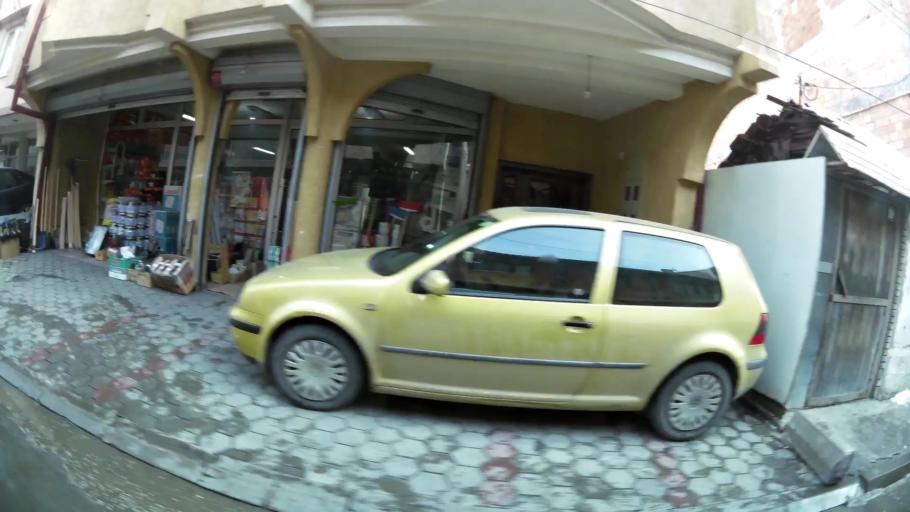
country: MK
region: Karpos
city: Skopje
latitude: 42.0042
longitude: 21.4360
